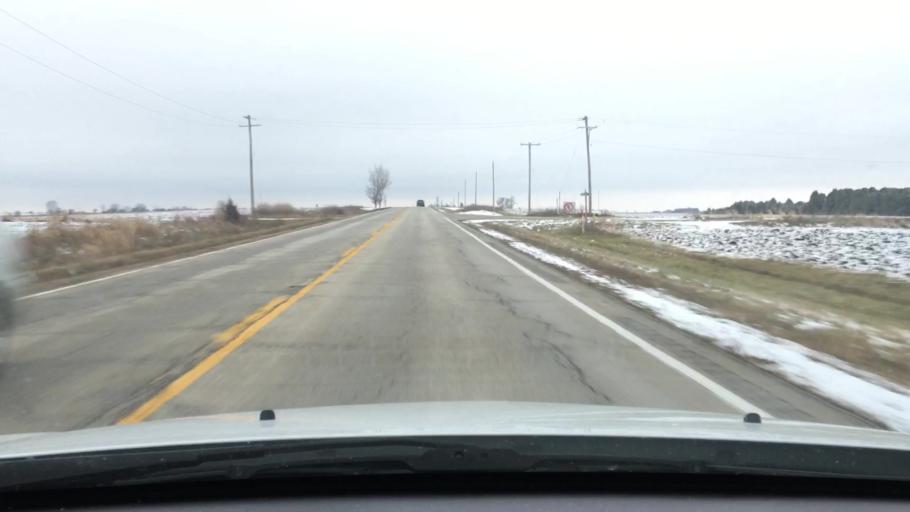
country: US
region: Illinois
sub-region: DeKalb County
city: Malta
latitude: 41.9355
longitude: -88.9251
